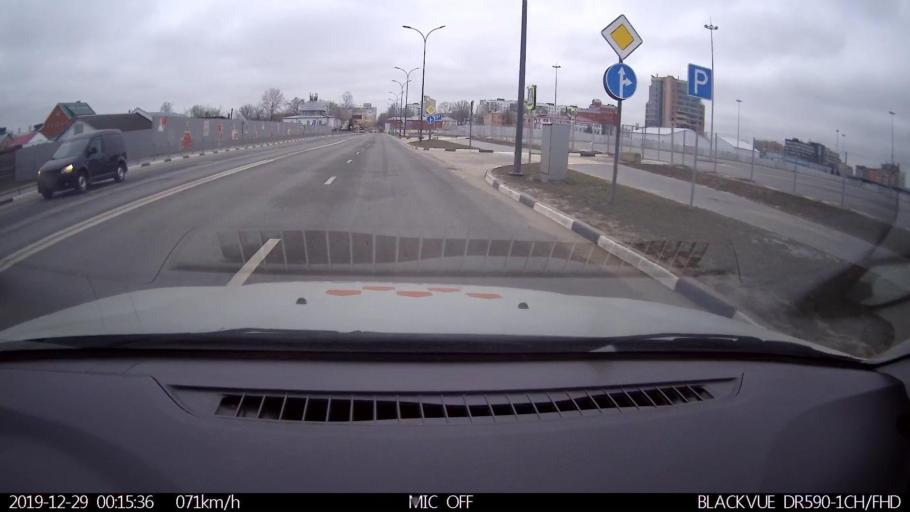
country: RU
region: Nizjnij Novgorod
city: Nizhniy Novgorod
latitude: 56.3338
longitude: 43.9685
